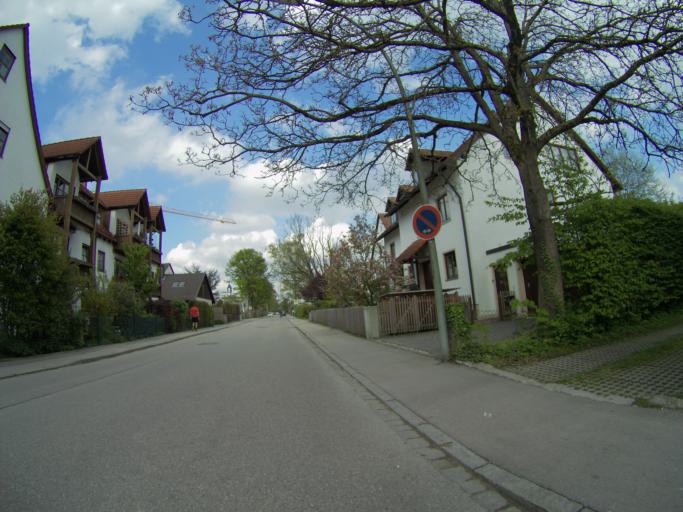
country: DE
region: Bavaria
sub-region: Upper Bavaria
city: Freising
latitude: 48.3921
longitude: 11.7542
